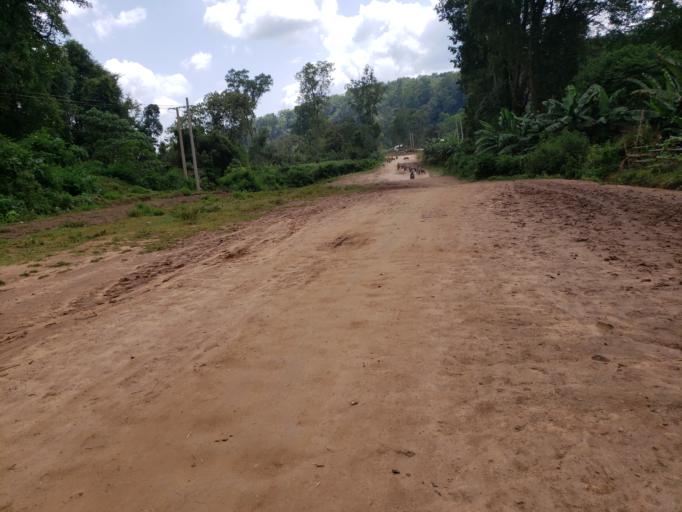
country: ET
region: Oromiya
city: Dodola
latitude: 6.4569
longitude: 39.5700
